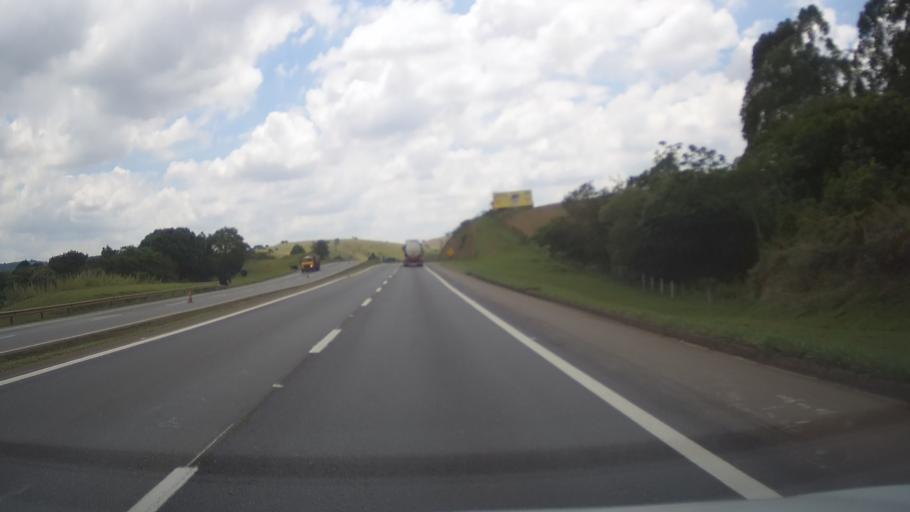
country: BR
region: Minas Gerais
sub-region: Campanha
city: Campanha
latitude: -21.7171
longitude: -45.3774
